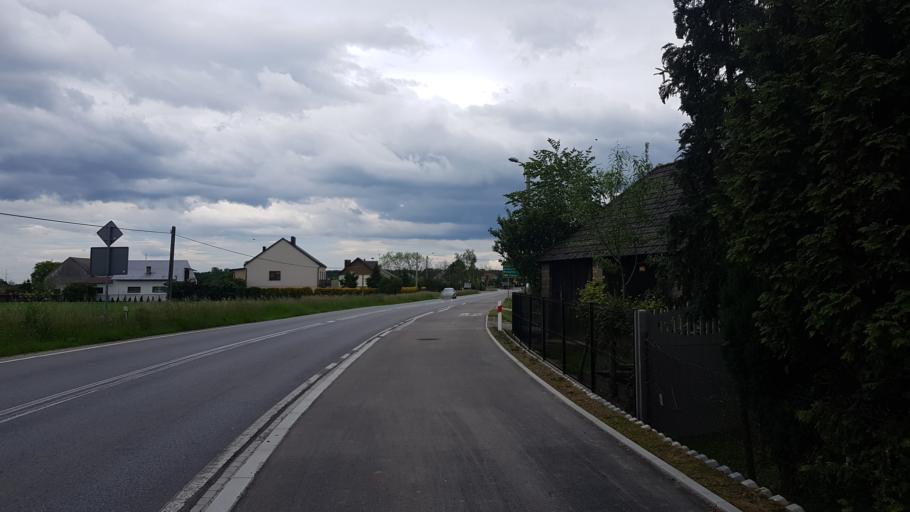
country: PL
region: Lesser Poland Voivodeship
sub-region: Powiat proszowicki
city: Nowe Brzesko
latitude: 50.1172
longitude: 20.3854
